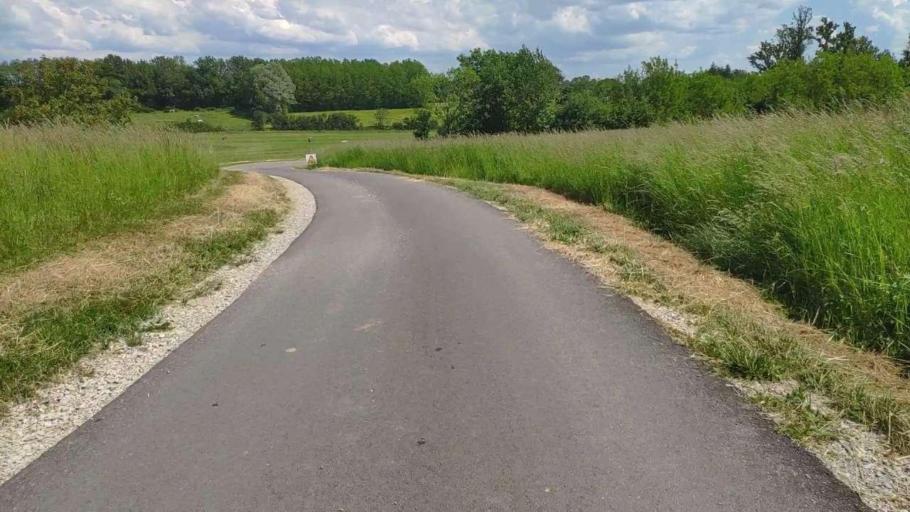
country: FR
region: Franche-Comte
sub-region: Departement du Jura
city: Bletterans
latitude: 46.7538
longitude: 5.3985
